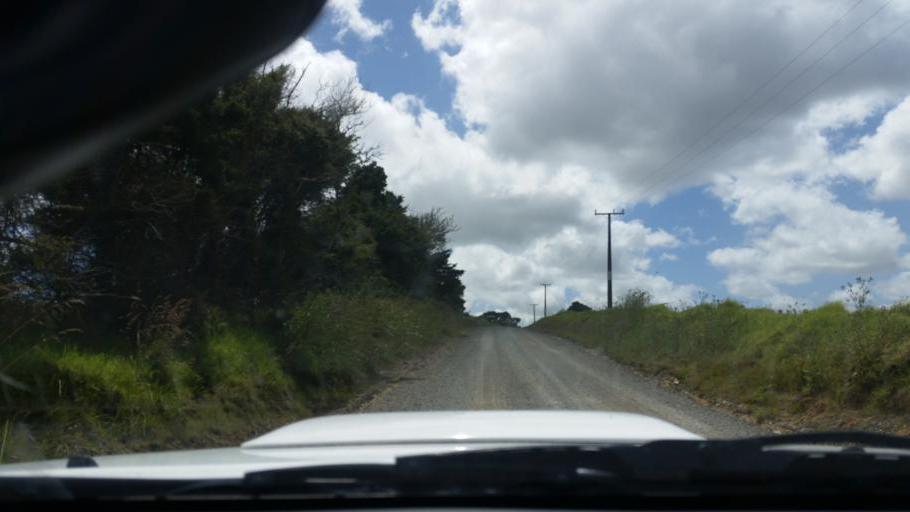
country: NZ
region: Northland
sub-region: Whangarei
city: Ruakaka
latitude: -36.0963
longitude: 174.2314
